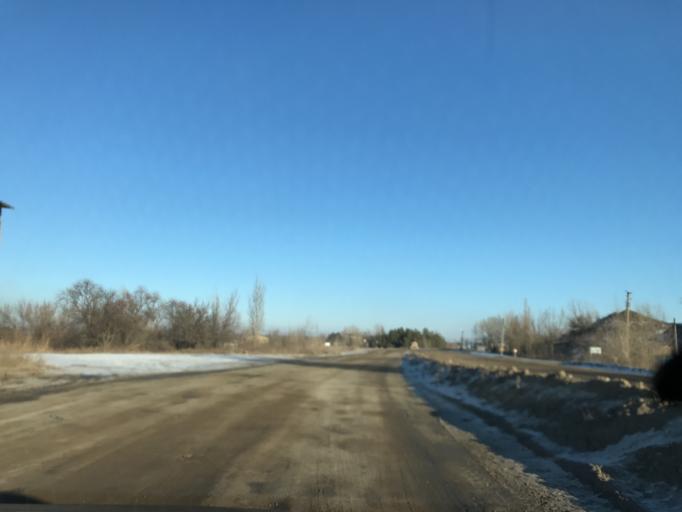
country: RU
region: Rostov
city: Staraya Stanitsa
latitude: 48.2372
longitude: 40.4022
